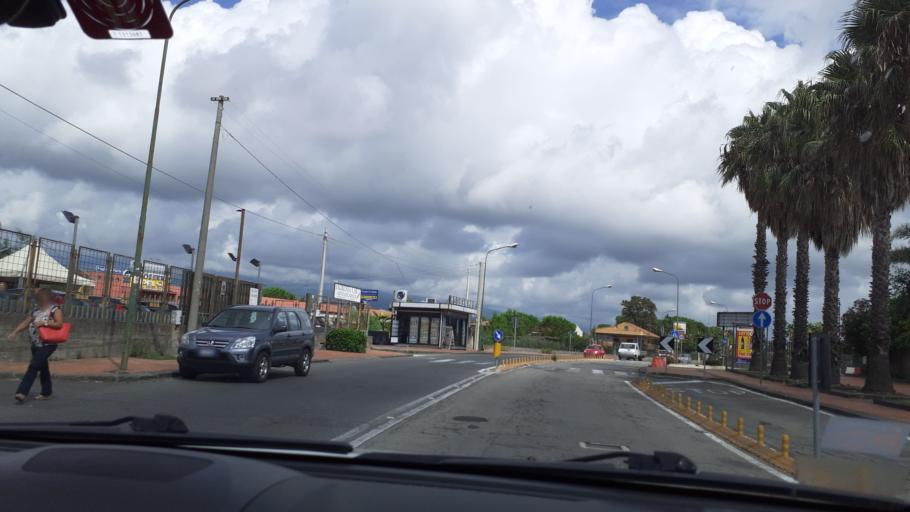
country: IT
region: Sicily
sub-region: Catania
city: San Gregorio di Catania
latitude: 37.5658
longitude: 15.1057
